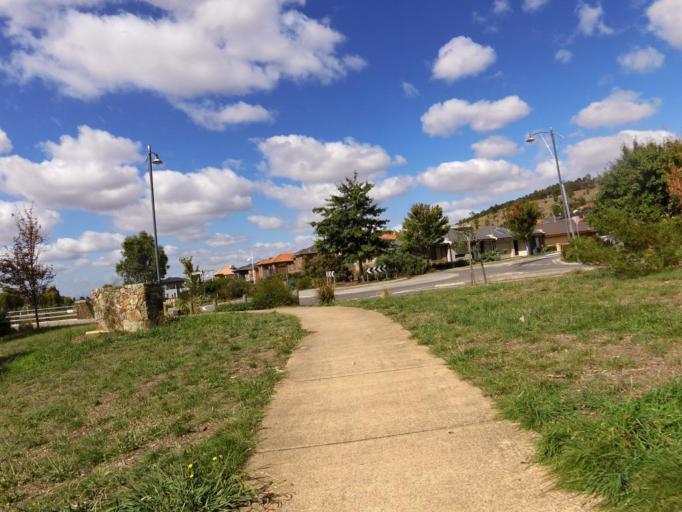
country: AU
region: Victoria
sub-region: Whittlesea
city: Mernda
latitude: -37.6250
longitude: 145.0679
